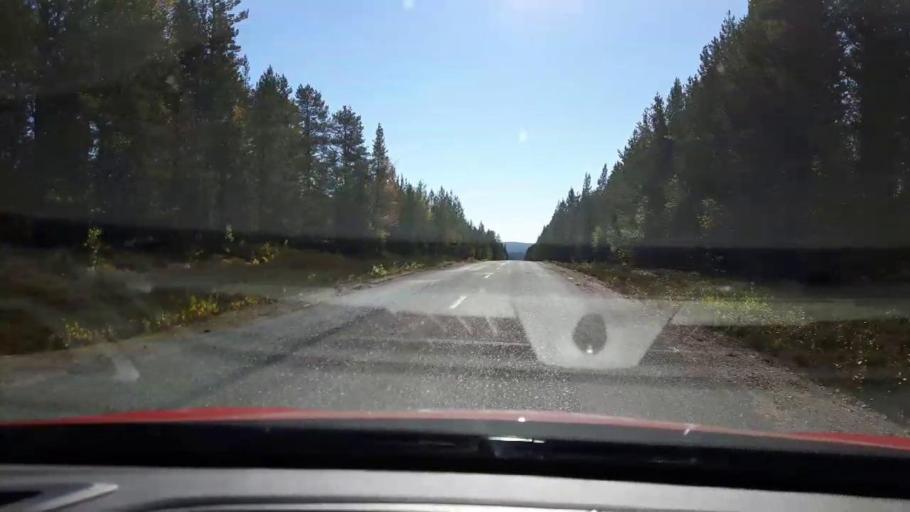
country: SE
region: Jaemtland
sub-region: Harjedalens Kommun
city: Sveg
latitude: 61.7292
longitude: 14.1654
